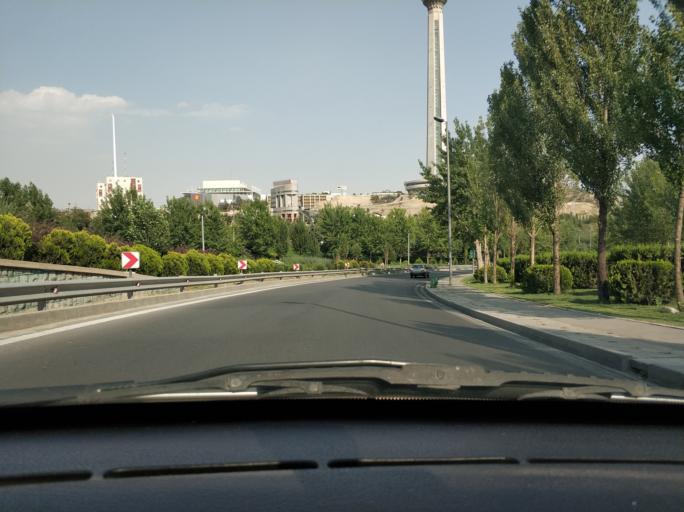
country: IR
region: Tehran
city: Tehran
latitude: 35.7486
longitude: 51.3690
